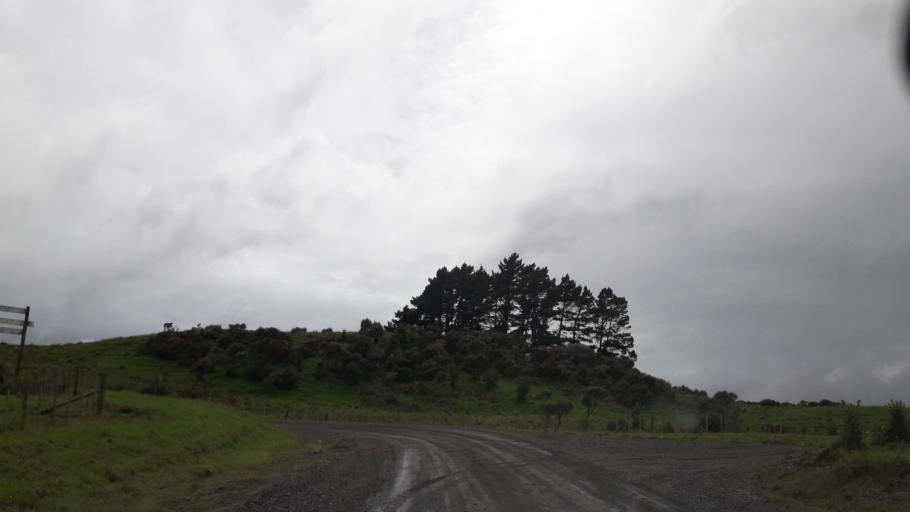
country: NZ
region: Northland
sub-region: Far North District
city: Kaitaia
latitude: -35.4143
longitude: 173.3662
